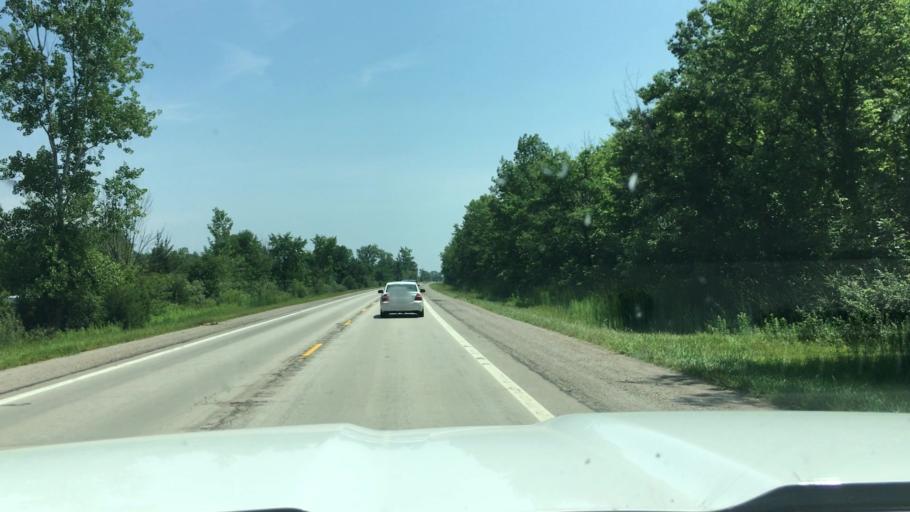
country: US
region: Michigan
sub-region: Shiawassee County
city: New Haven
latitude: 43.1869
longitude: -84.2742
